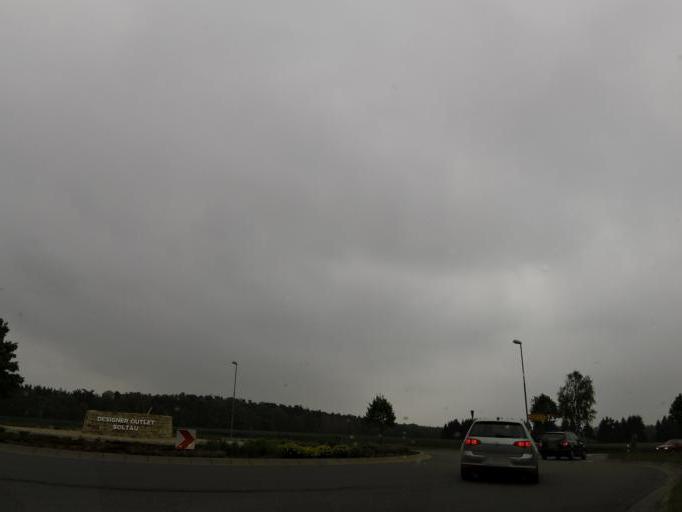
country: DE
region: Lower Saxony
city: Soltau
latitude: 52.9886
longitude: 9.9199
